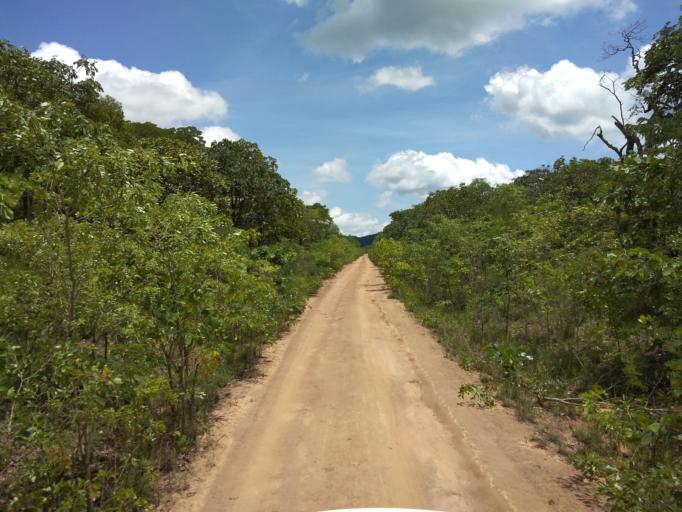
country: ZM
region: Central
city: Mkushi
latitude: -13.9608
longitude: 29.9284
